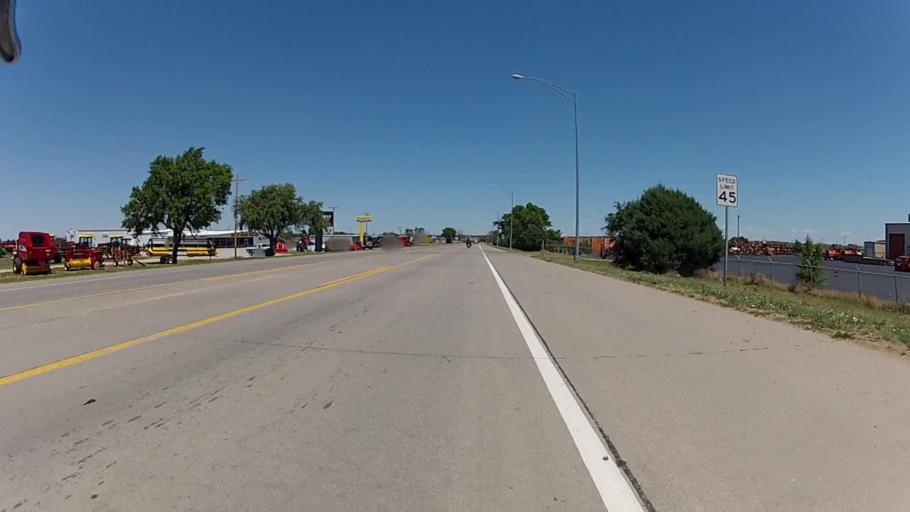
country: US
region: Kansas
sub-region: Ford County
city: Dodge City
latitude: 37.7257
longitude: -100.0165
